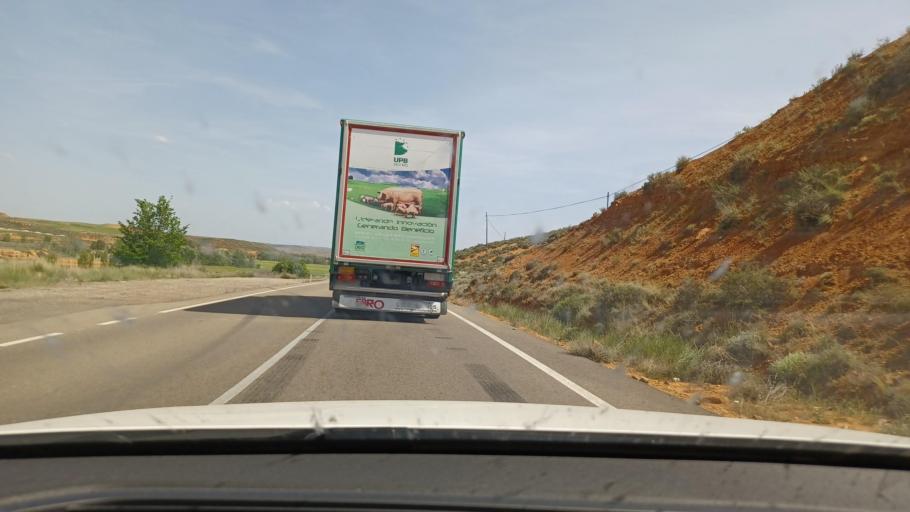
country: ES
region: Aragon
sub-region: Provincia de Zaragoza
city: Pozuel de Ariza
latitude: 41.3287
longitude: -2.1491
